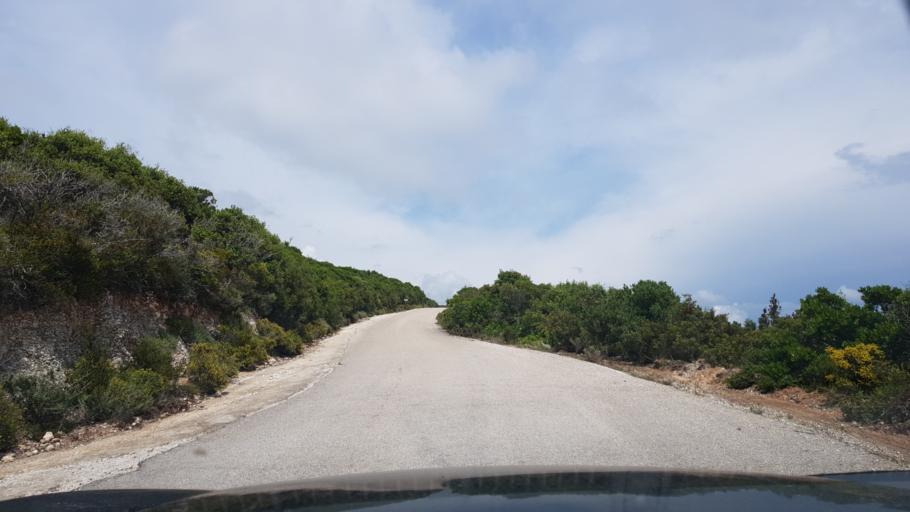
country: GR
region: Ionian Islands
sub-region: Lefkada
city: Nidri
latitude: 38.5950
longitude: 20.5522
